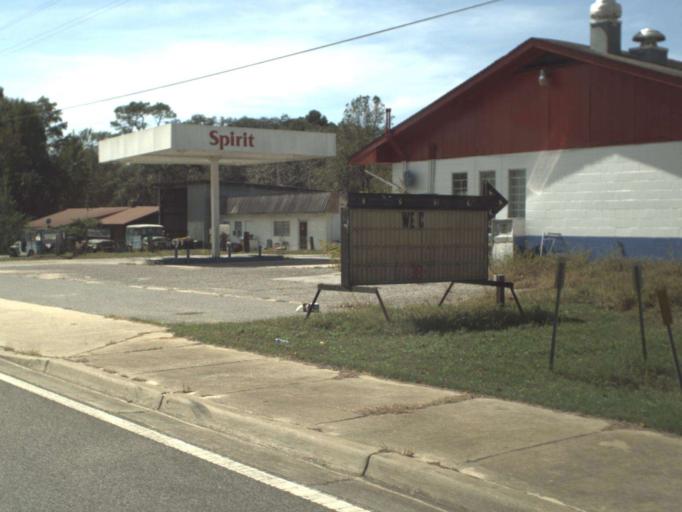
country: US
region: Florida
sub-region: Washington County
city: Chipley
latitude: 30.6277
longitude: -85.5914
